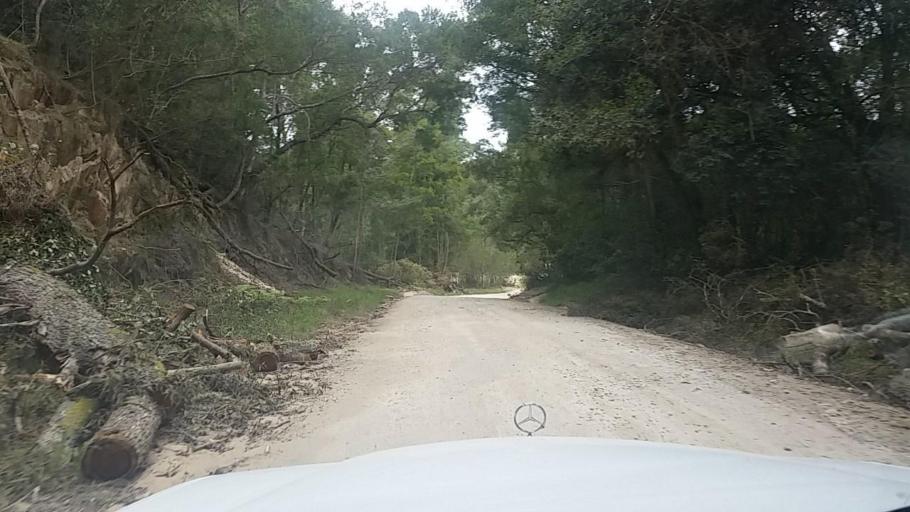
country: ZA
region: Western Cape
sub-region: Eden District Municipality
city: Knysna
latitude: -34.0037
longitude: 23.1183
